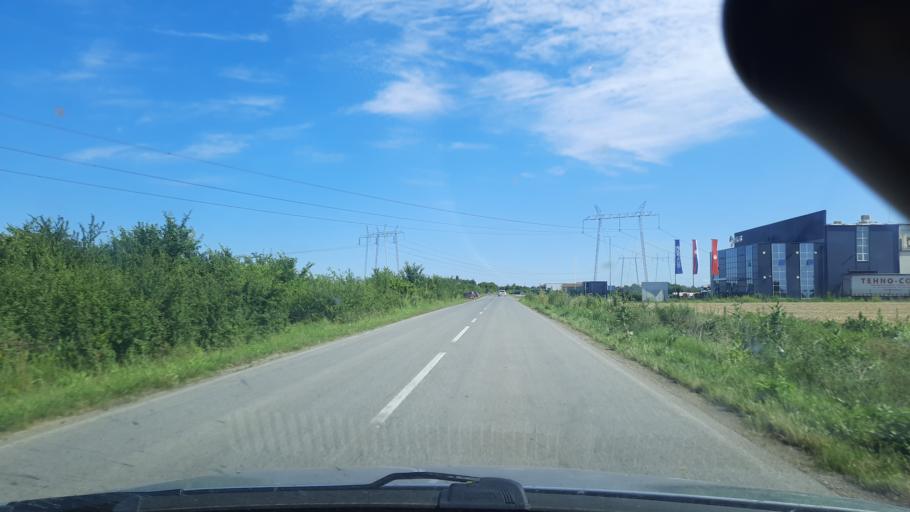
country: RS
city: Simanovci
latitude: 44.8506
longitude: 20.1009
